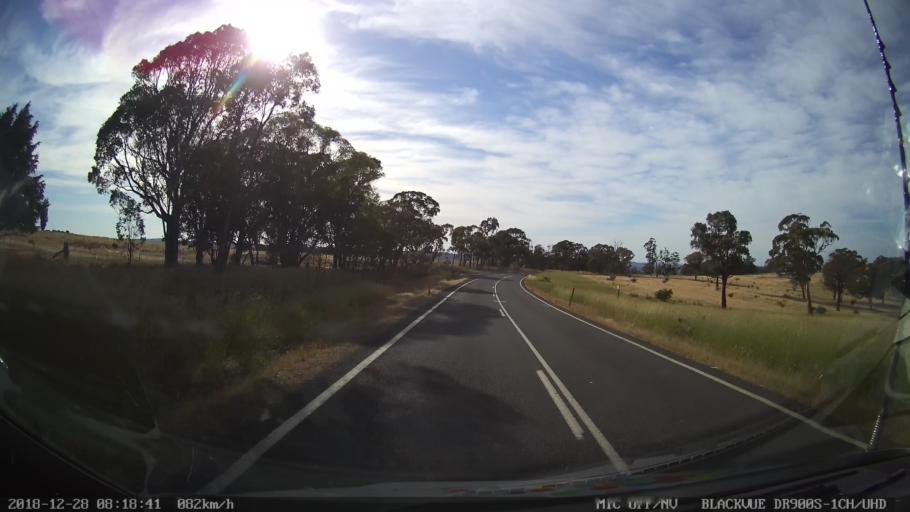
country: AU
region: New South Wales
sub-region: Blayney
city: Blayney
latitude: -33.8500
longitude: 149.3494
